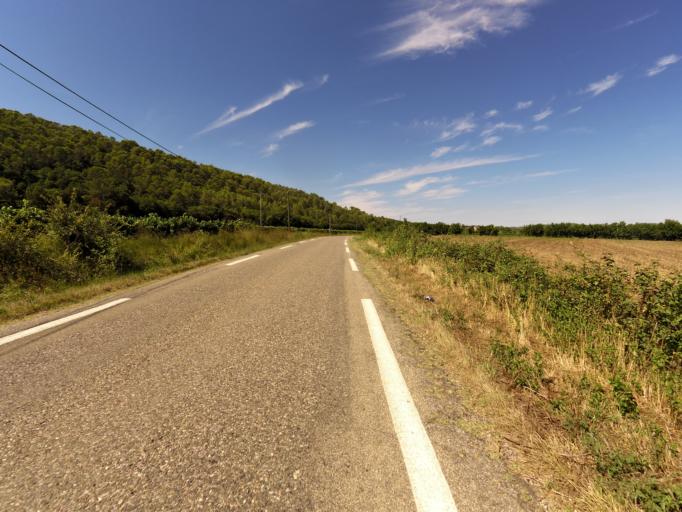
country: FR
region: Languedoc-Roussillon
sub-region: Departement du Gard
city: Quissac
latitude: 43.8628
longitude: 4.0405
